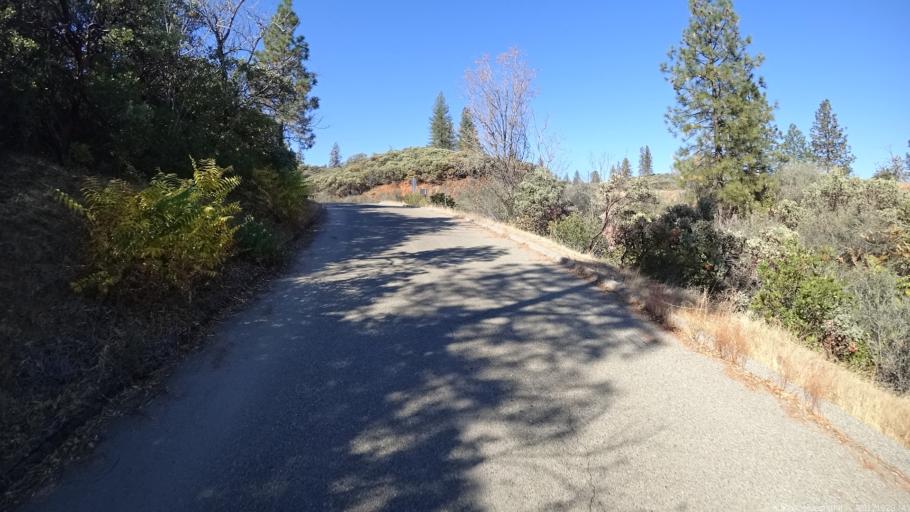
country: US
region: California
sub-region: Shasta County
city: Shasta
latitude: 40.6321
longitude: -122.4530
